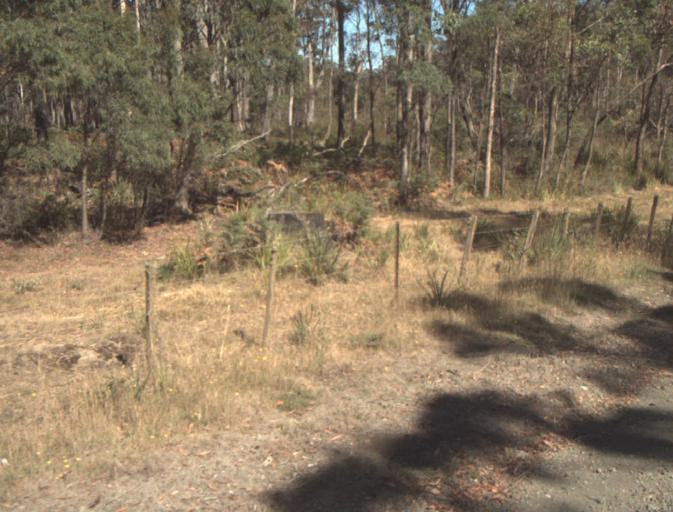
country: AU
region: Tasmania
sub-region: Launceston
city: Newstead
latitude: -41.3722
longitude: 147.2800
